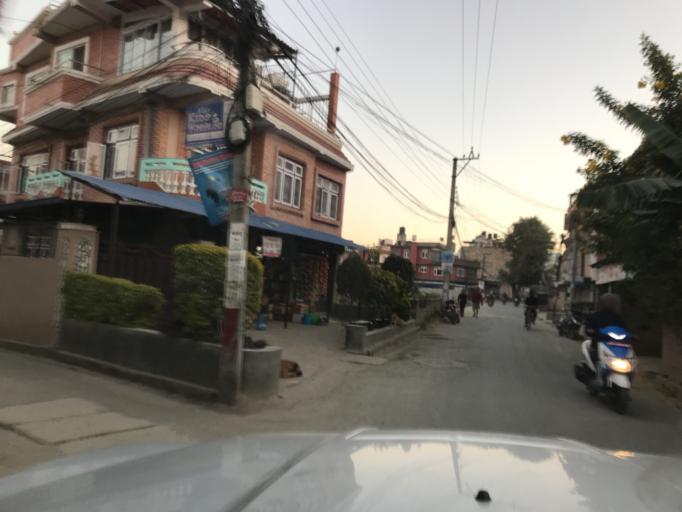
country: NP
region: Central Region
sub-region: Bagmati Zone
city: Patan
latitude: 27.6548
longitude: 85.3170
